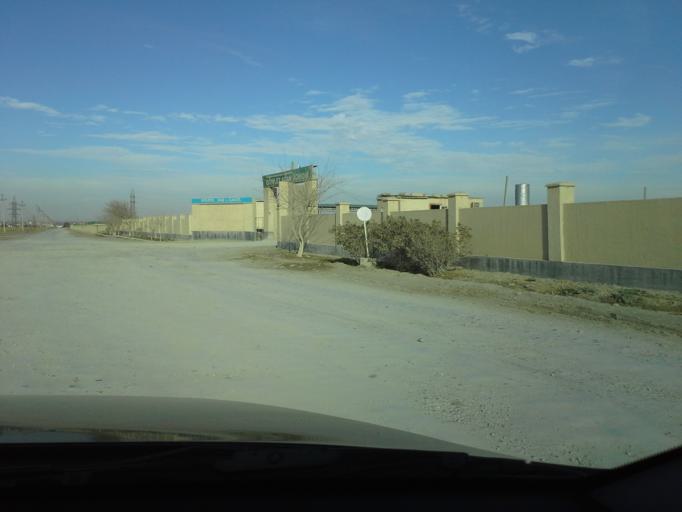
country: TM
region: Ahal
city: Abadan
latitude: 38.0383
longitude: 58.1616
